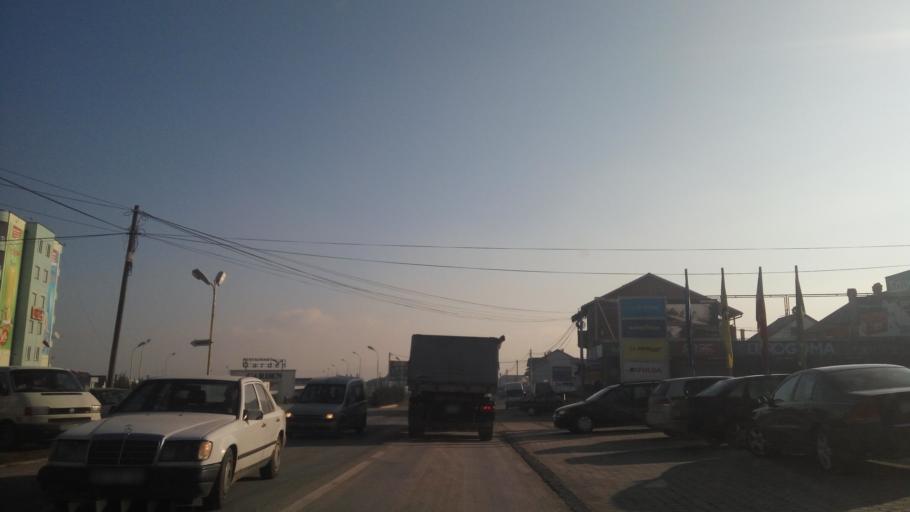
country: XK
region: Gjilan
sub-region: Komuna e Gjilanit
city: Gjilan
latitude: 42.4690
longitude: 21.4392
